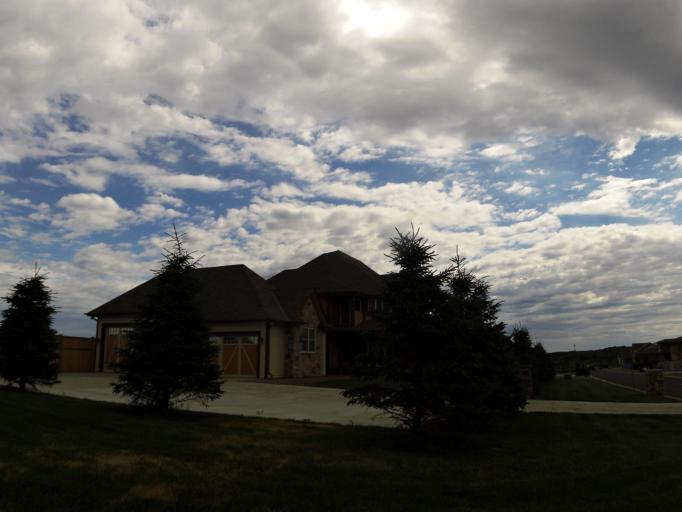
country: US
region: Minnesota
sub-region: Scott County
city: Prior Lake
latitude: 44.7606
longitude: -93.4444
